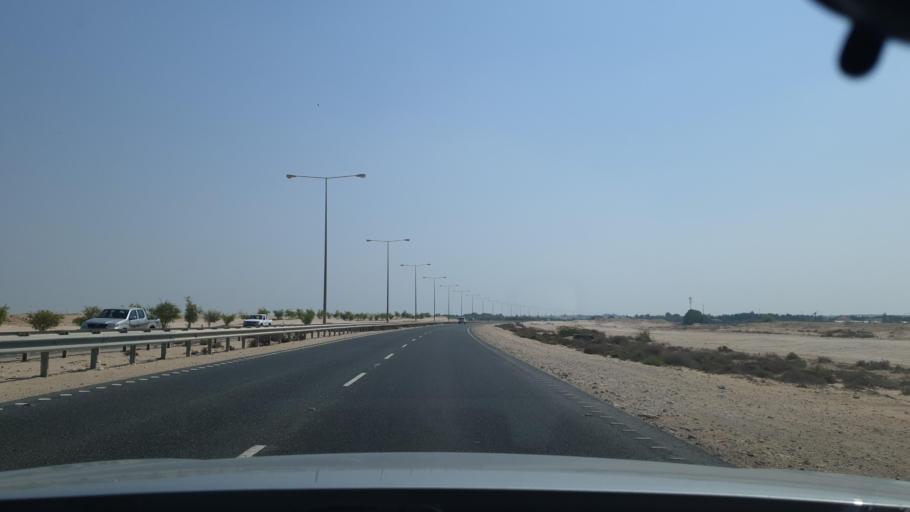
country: QA
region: Al Khawr
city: Al Khawr
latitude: 25.7375
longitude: 51.4901
